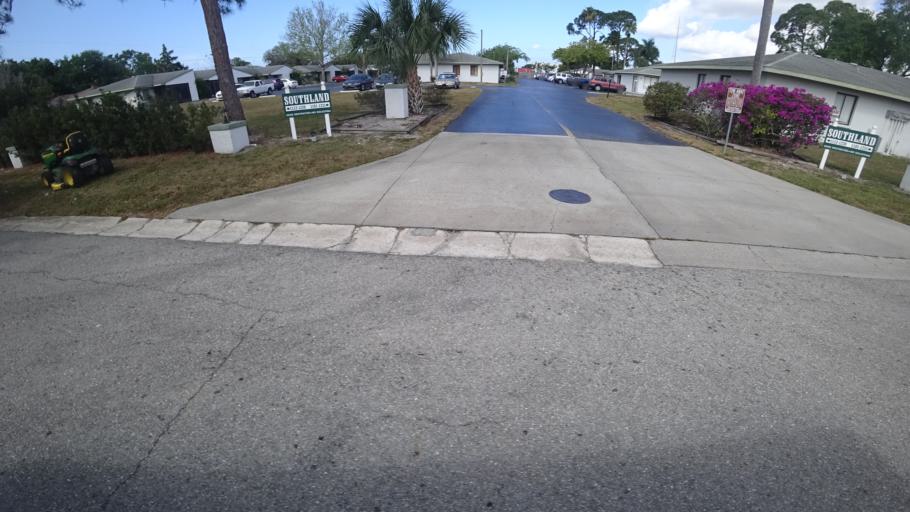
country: US
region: Florida
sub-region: Manatee County
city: Whitfield
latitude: 27.4194
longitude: -82.5733
